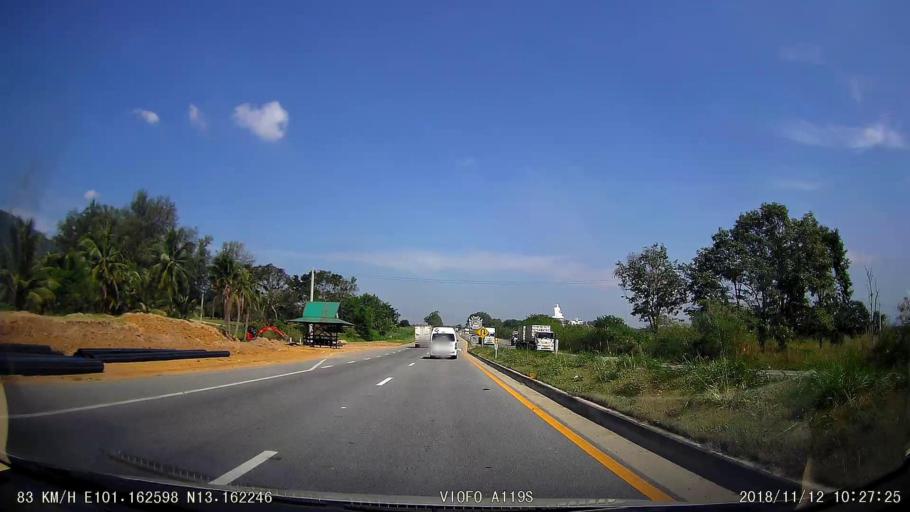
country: TH
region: Chon Buri
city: Ban Bueng
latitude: 13.1546
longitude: 101.1632
